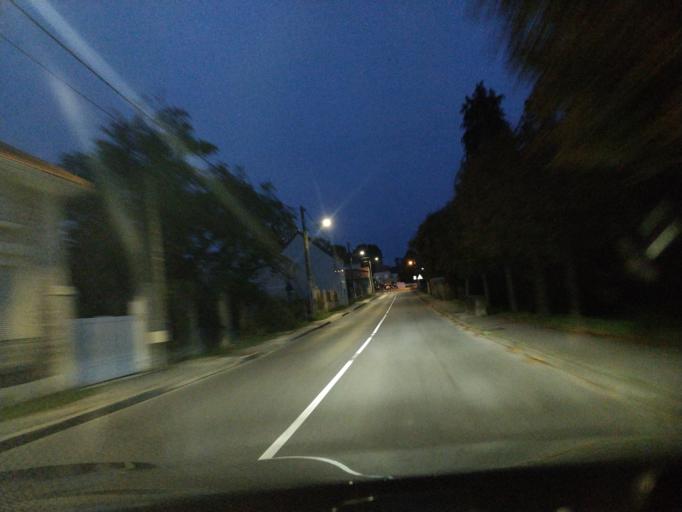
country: FR
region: Ile-de-France
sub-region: Departement de l'Essonne
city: Forges-les-Bains
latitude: 48.6289
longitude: 2.0960
